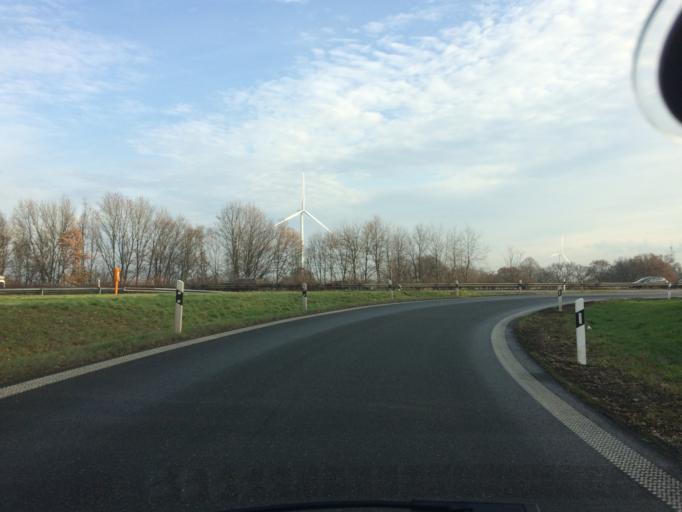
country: DE
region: North Rhine-Westphalia
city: Dorsten
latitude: 51.6300
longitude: 6.9325
